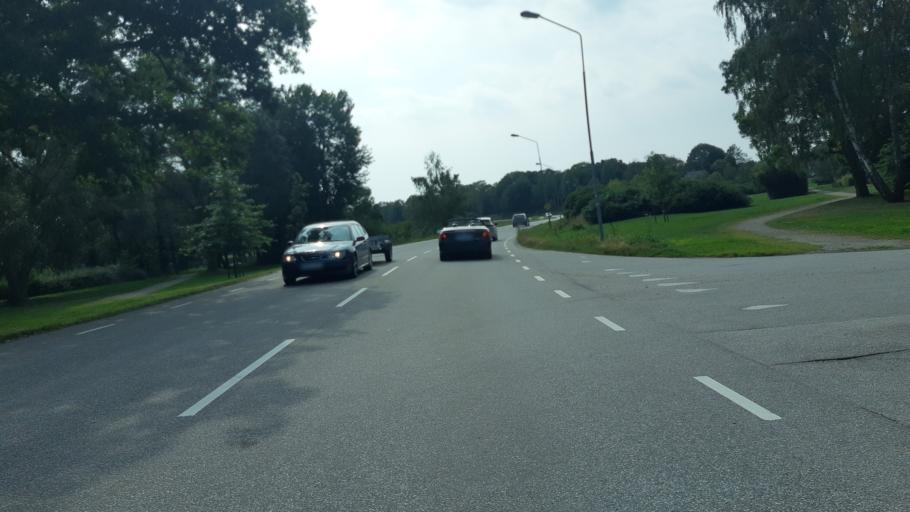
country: SE
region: Blekinge
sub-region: Karlskrona Kommun
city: Nattraby
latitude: 56.1990
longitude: 15.5363
